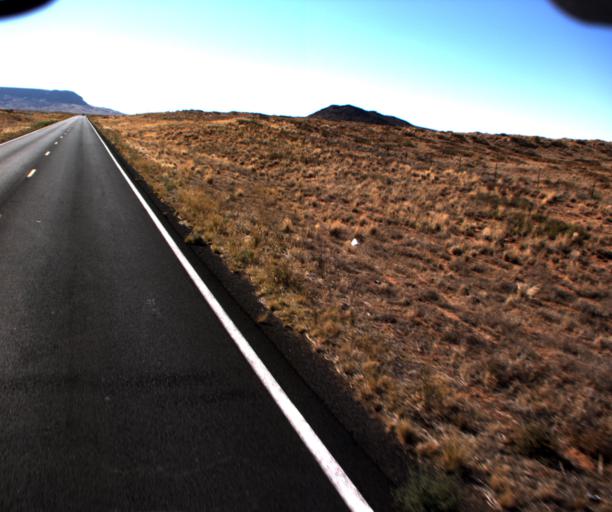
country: US
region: Arizona
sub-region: Navajo County
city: Dilkon
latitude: 35.4760
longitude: -110.4256
